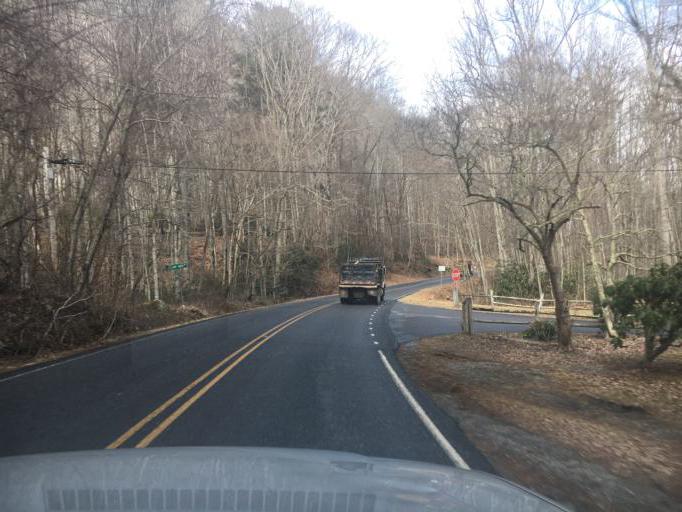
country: US
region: North Carolina
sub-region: Haywood County
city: Canton
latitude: 35.3838
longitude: -82.8151
